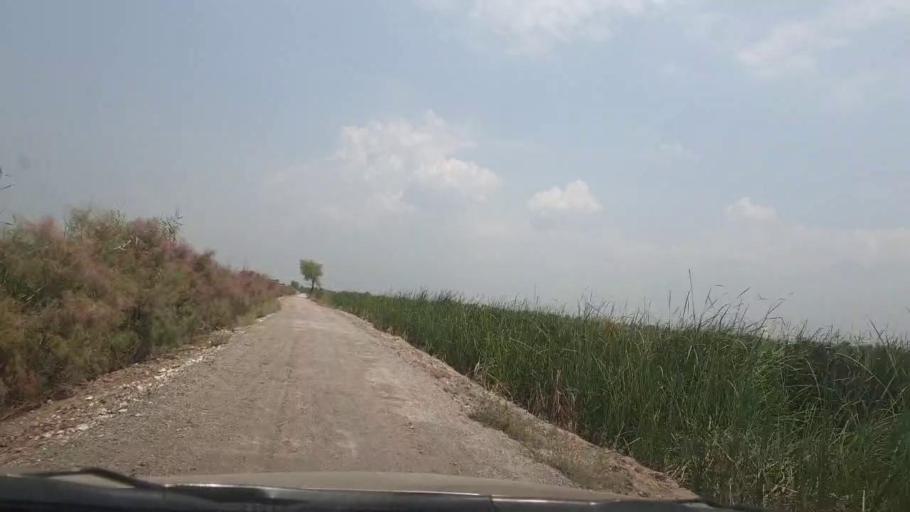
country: PK
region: Sindh
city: Naudero
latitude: 27.7223
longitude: 68.3255
